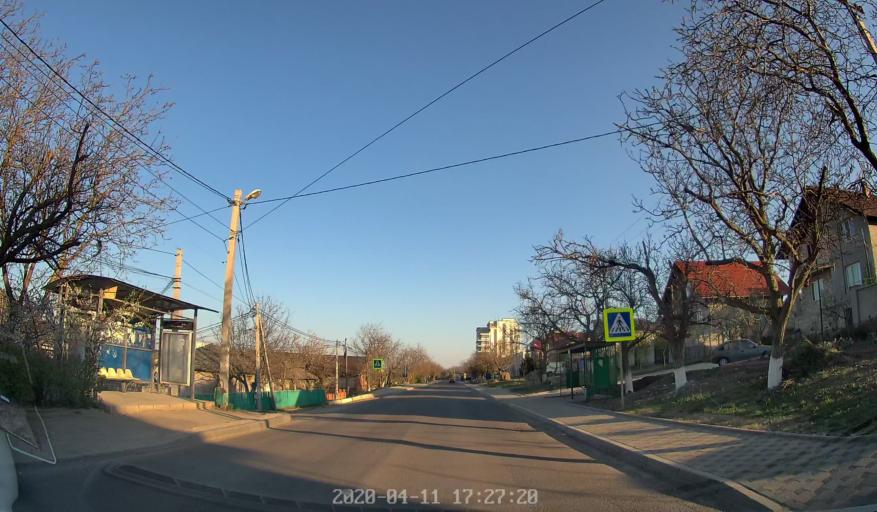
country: MD
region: Laloveni
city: Ialoveni
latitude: 47.0094
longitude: 28.7622
